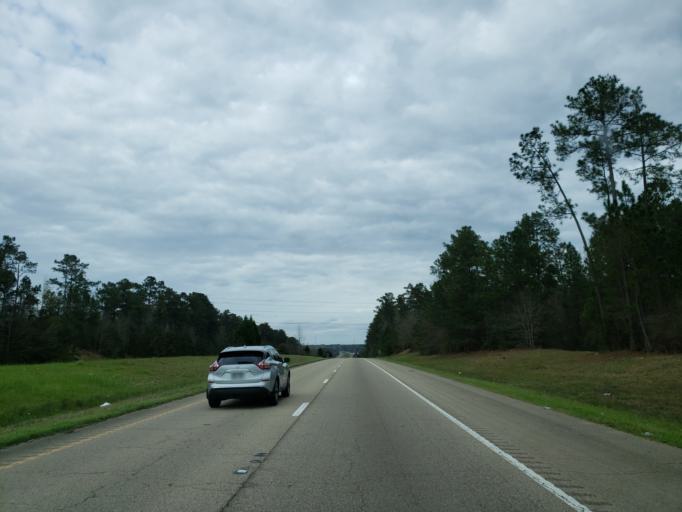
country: US
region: Mississippi
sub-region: Lamar County
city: Purvis
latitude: 31.1571
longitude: -89.3586
